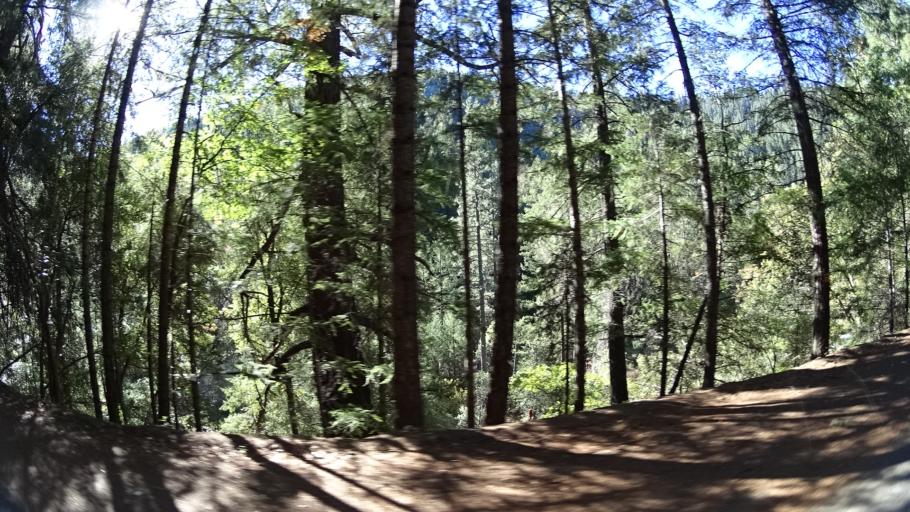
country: US
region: California
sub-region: Trinity County
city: Weaverville
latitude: 41.1431
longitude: -123.1821
